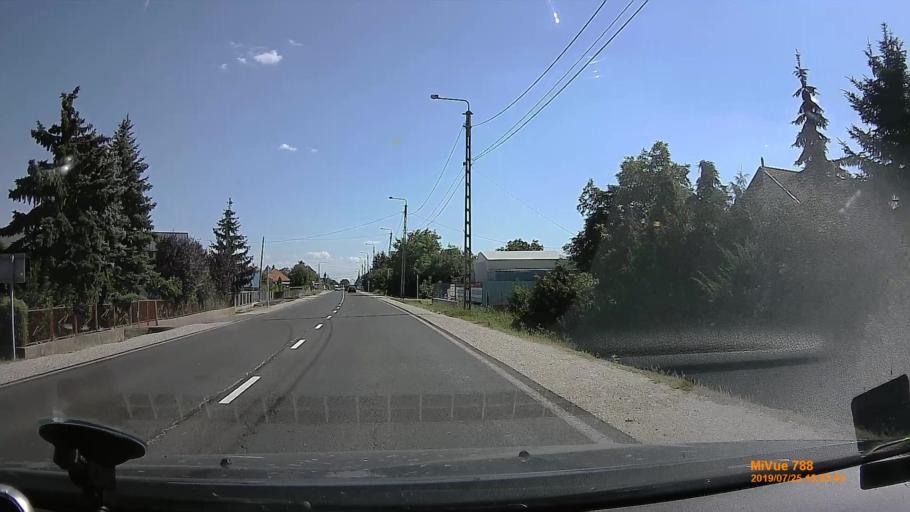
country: HU
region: Borsod-Abauj-Zemplen
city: Nyekladhaza
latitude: 47.9927
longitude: 20.8302
